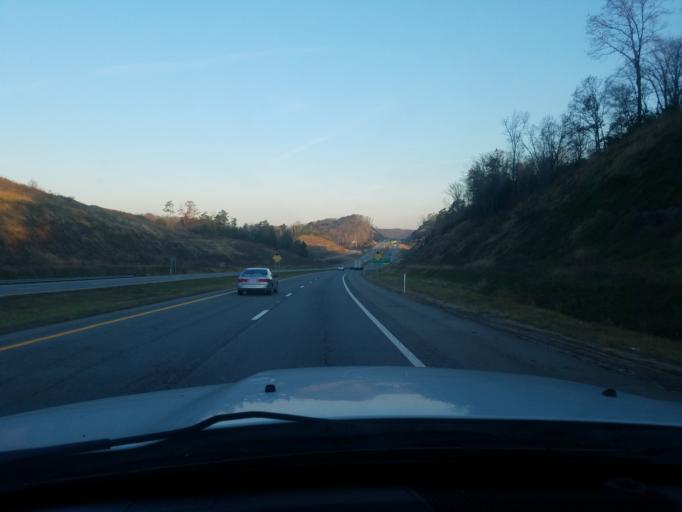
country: US
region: West Virginia
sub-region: Putnam County
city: Buffalo
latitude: 38.5630
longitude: -82.0116
